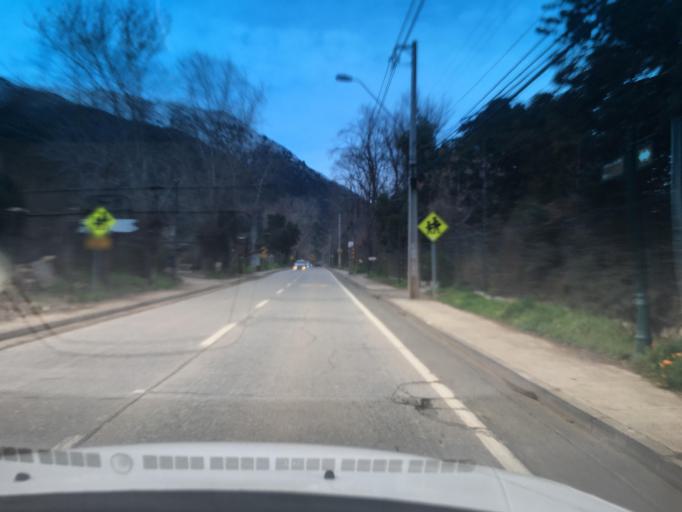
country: CL
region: Santiago Metropolitan
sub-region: Provincia de Cordillera
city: Puente Alto
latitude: -33.5768
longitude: -70.4539
